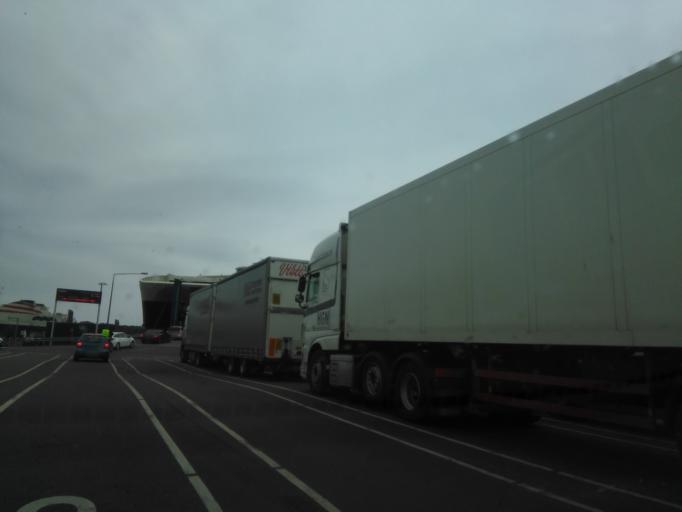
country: DK
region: Capital Region
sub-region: Bornholm Kommune
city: Ronne
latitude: 55.1004
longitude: 14.6909
